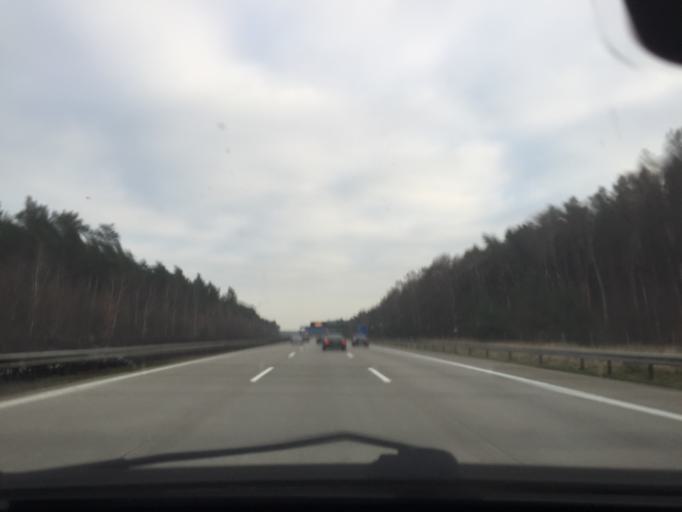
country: DE
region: Brandenburg
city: Gross Kreutz
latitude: 52.3394
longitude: 12.7839
